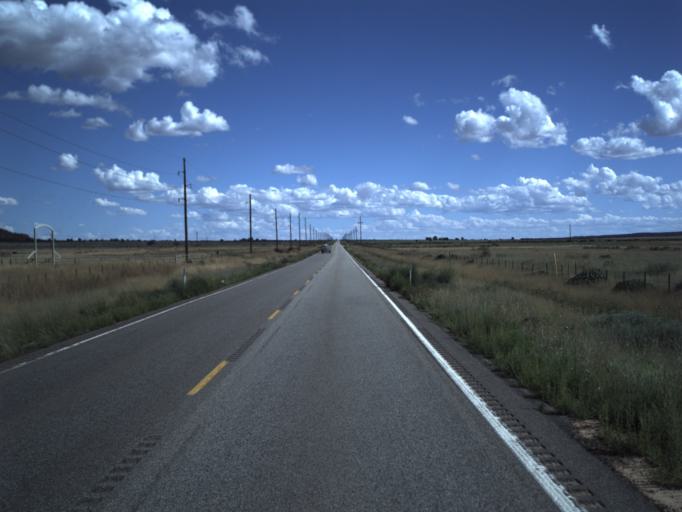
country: US
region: Arizona
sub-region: Mohave County
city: Colorado City
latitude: 37.0880
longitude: -113.1132
